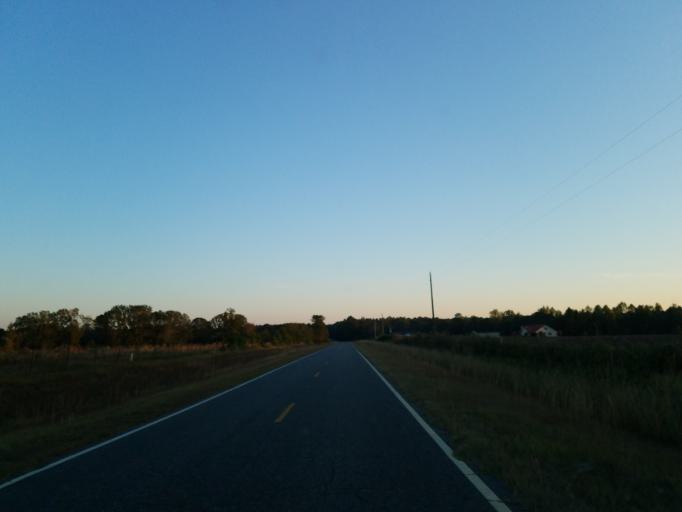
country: US
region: Georgia
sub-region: Ben Hill County
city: Fitzgerald
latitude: 31.6887
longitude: -83.4111
